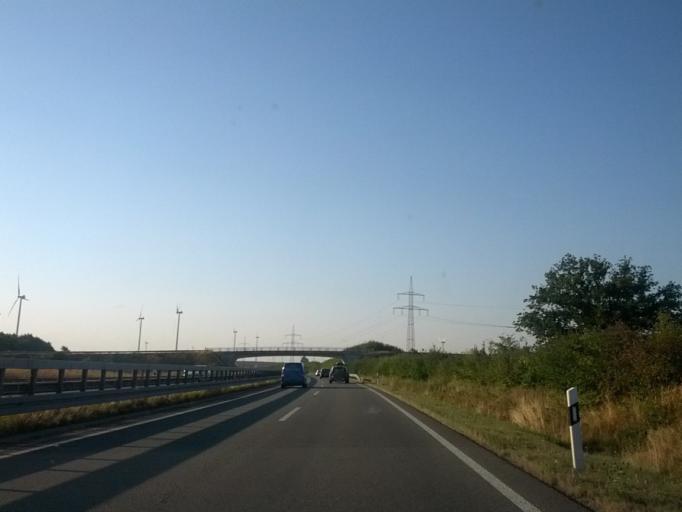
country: DE
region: Mecklenburg-Vorpommern
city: Brandshagen
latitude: 54.2074
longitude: 13.1515
